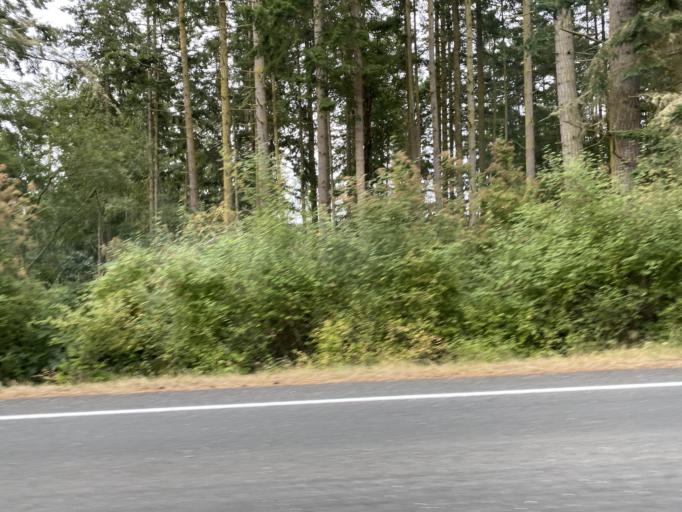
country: US
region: Washington
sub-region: Island County
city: Coupeville
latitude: 48.2319
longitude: -122.7466
